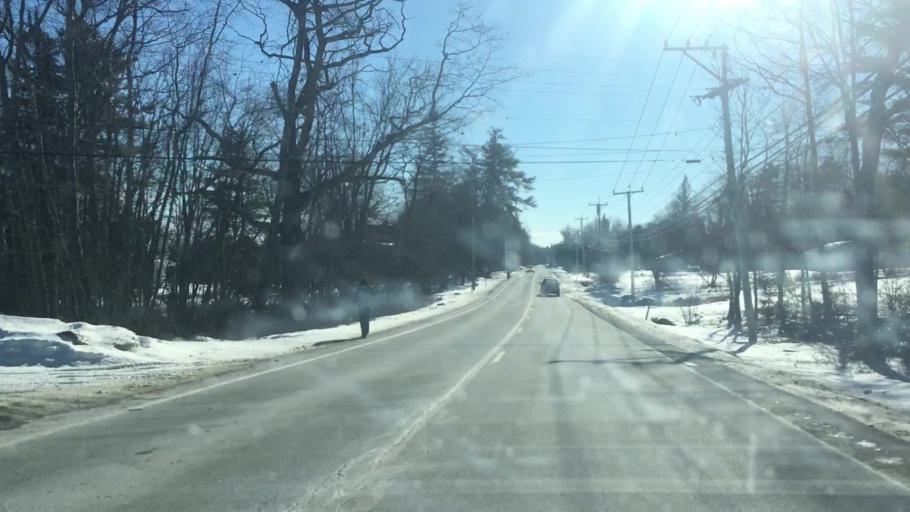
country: US
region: Maine
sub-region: Hancock County
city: Ellsworth
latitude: 44.5282
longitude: -68.4322
